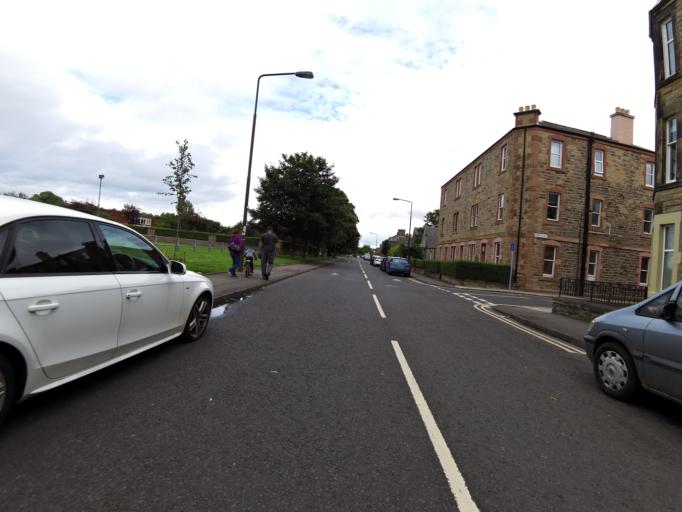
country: GB
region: Scotland
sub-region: East Lothian
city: Musselburgh
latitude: 55.9454
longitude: -3.0564
